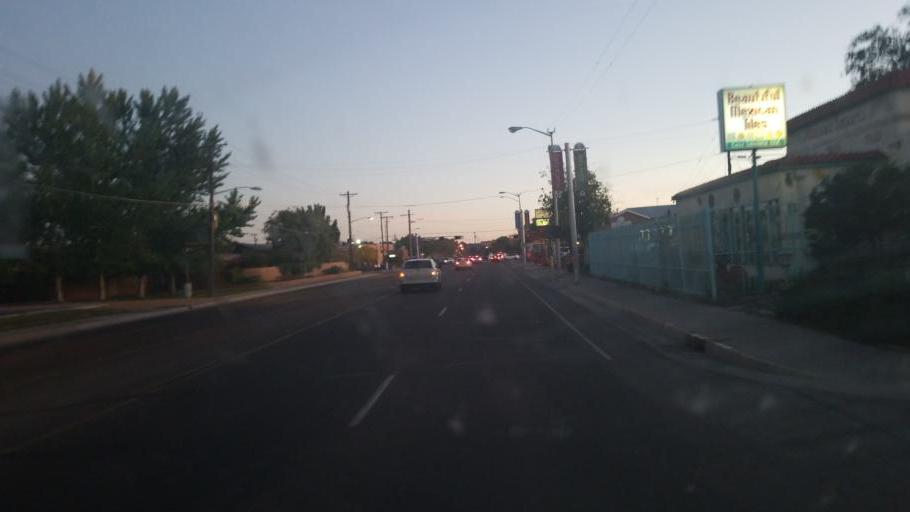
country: US
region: New Mexico
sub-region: Bernalillo County
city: Albuquerque
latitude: 35.1001
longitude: -106.6707
